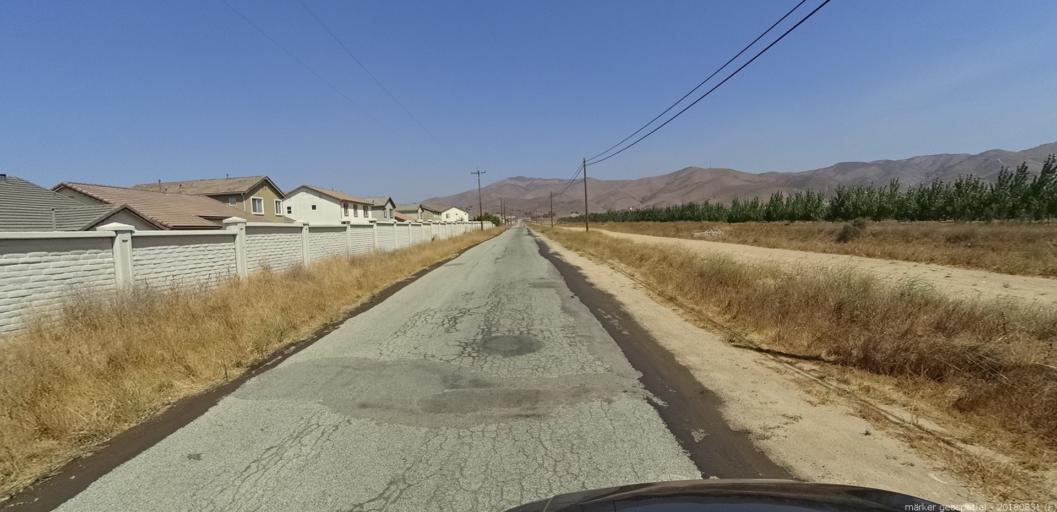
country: US
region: California
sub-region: Monterey County
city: Soledad
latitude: 36.4332
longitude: -121.3112
